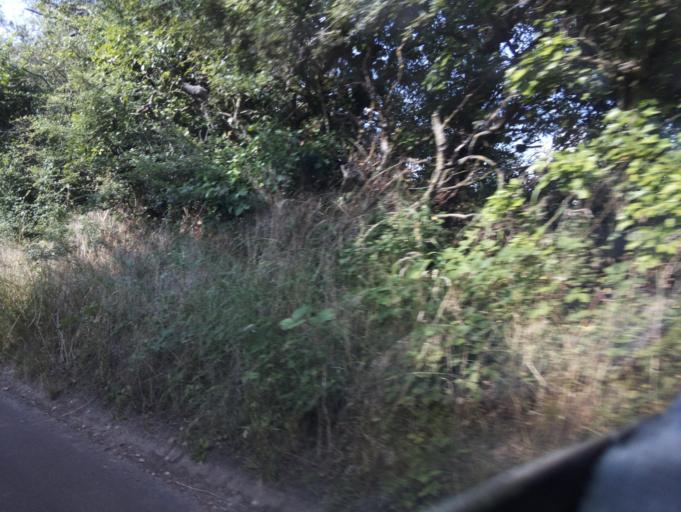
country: GB
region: England
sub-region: Wiltshire
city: Minety
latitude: 51.6257
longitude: -1.9710
